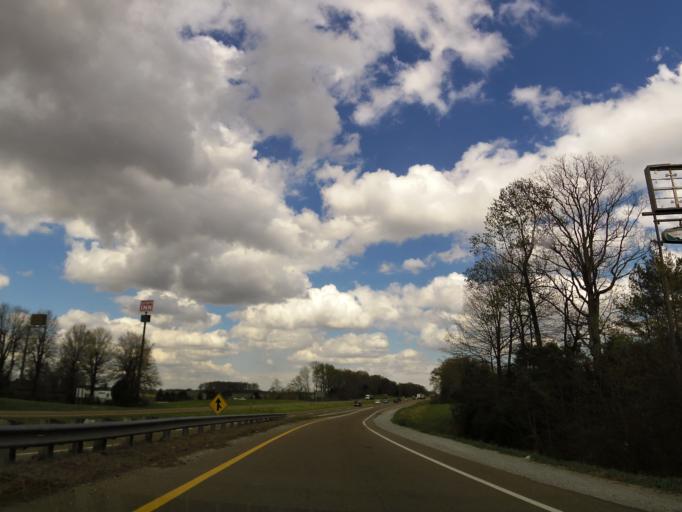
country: US
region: Tennessee
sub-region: Crockett County
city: Bells
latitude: 35.5968
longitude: -89.0540
